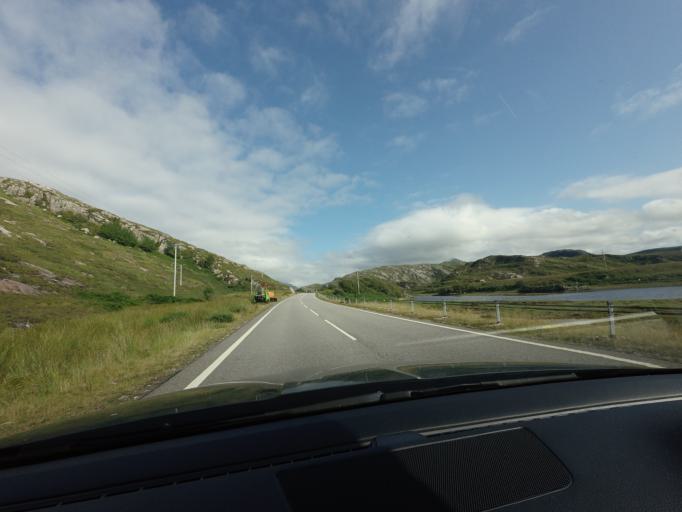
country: GB
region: Scotland
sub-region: Highland
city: Ullapool
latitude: 58.3791
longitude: -5.0259
